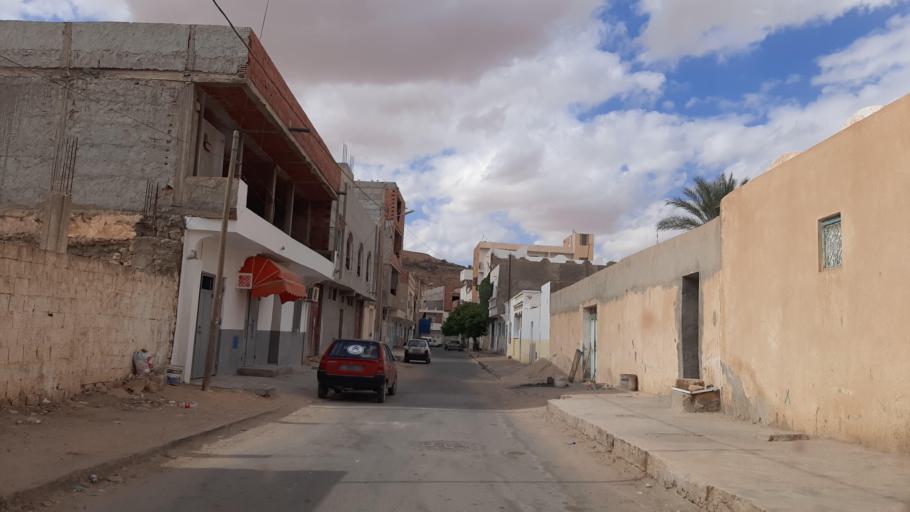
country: TN
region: Tataouine
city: Tataouine
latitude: 32.9309
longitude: 10.4487
